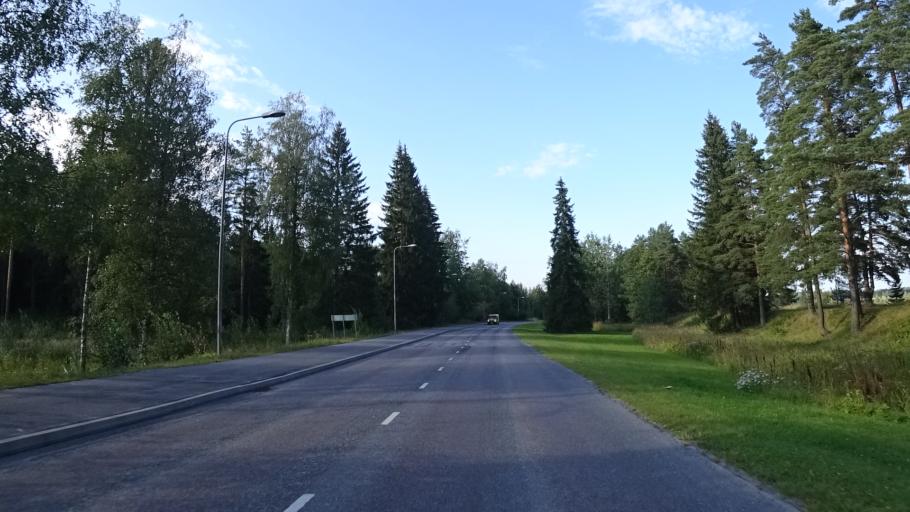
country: FI
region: South Karelia
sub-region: Imatra
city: Imatra
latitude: 61.1749
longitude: 28.7777
